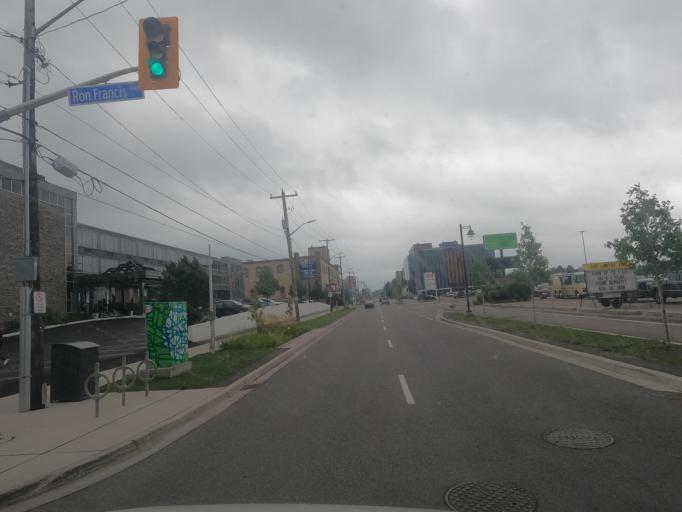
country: CA
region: Ontario
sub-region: Algoma
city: Sault Ste. Marie
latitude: 46.5127
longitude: -84.3370
